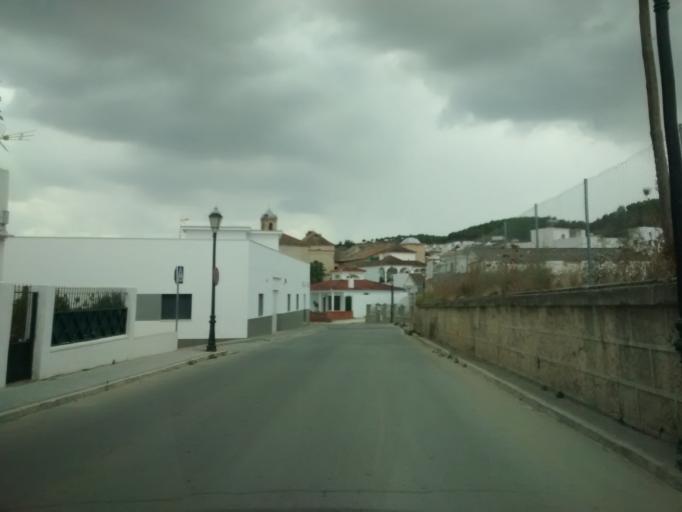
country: ES
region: Andalusia
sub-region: Provincia de Cadiz
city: Bornos
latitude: 36.8184
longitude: -5.7455
